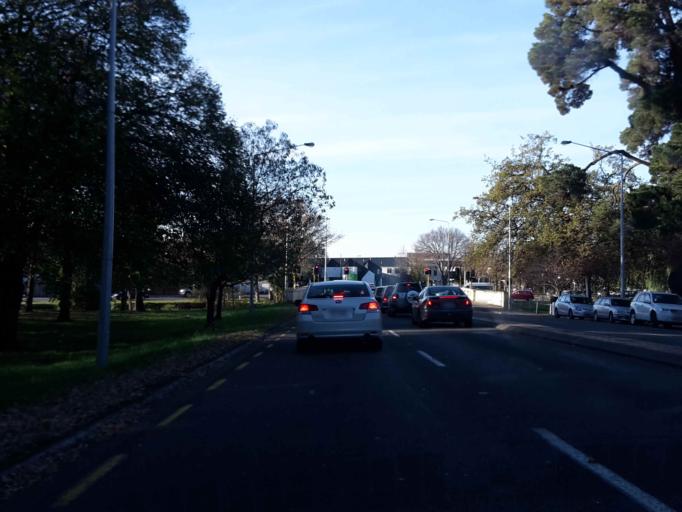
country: NZ
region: Canterbury
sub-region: Christchurch City
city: Christchurch
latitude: -43.5216
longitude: 172.6246
